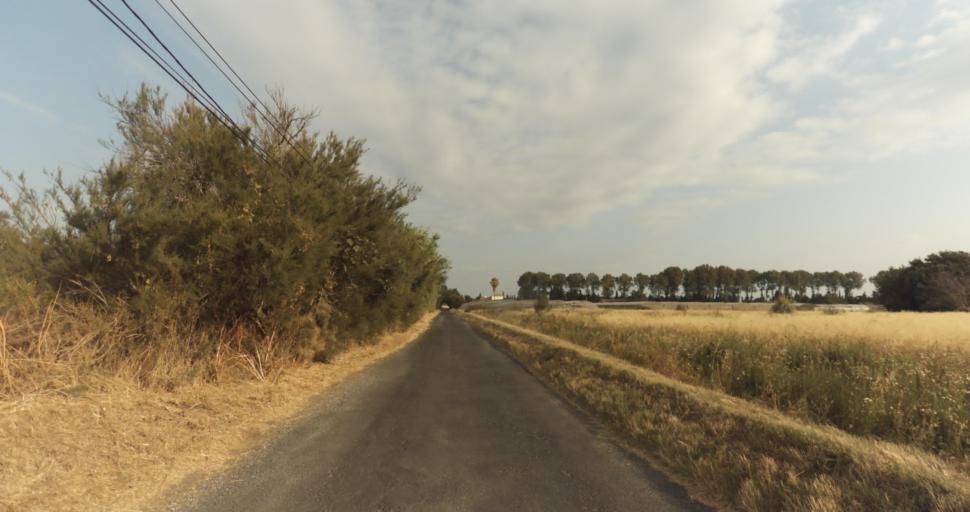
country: FR
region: Languedoc-Roussillon
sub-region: Departement des Pyrenees-Orientales
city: Theza
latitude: 42.6330
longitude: 2.9463
